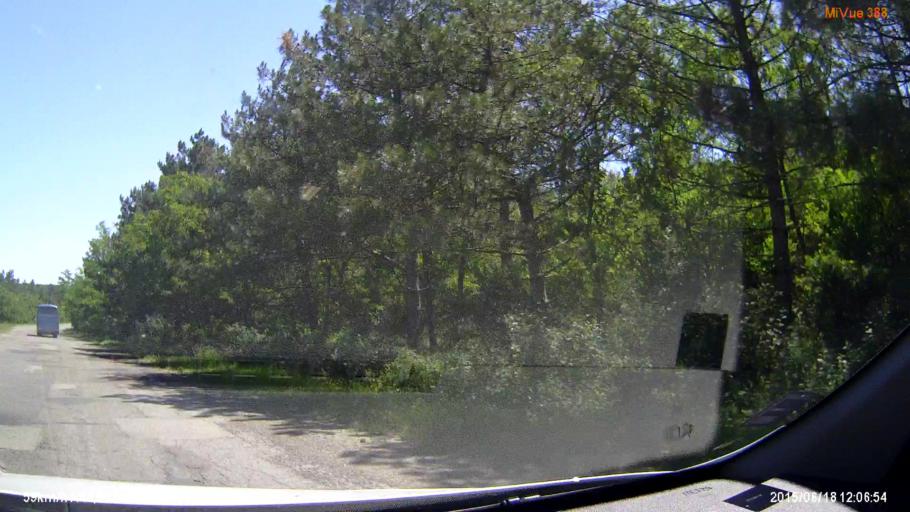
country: MD
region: Cimislia
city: Cimislia
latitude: 46.5414
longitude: 28.9048
